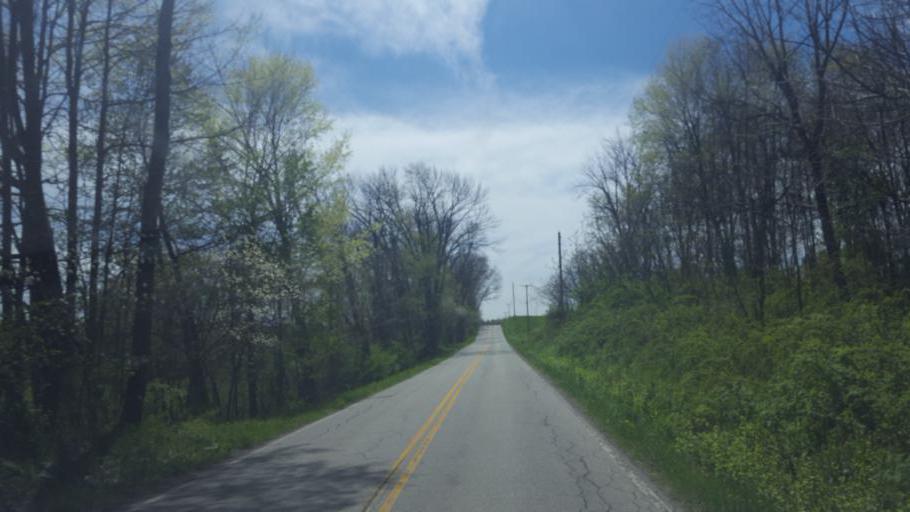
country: US
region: Ohio
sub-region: Richland County
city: Lincoln Heights
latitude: 40.6961
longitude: -82.4363
